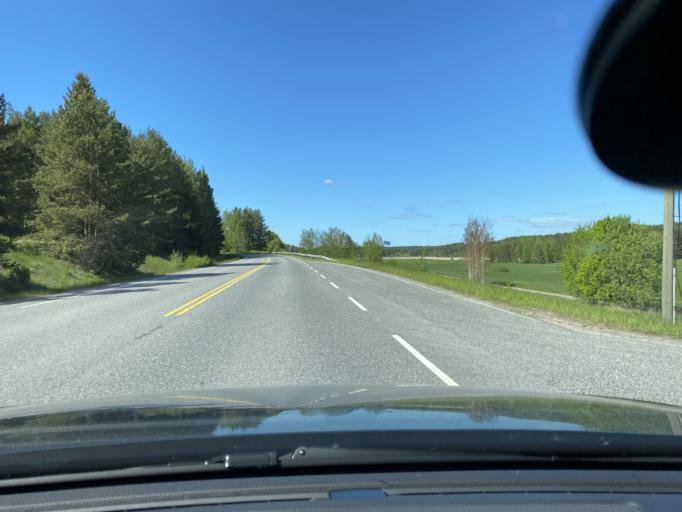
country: FI
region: Varsinais-Suomi
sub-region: Turku
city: Sauvo
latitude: 60.3729
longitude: 22.6705
